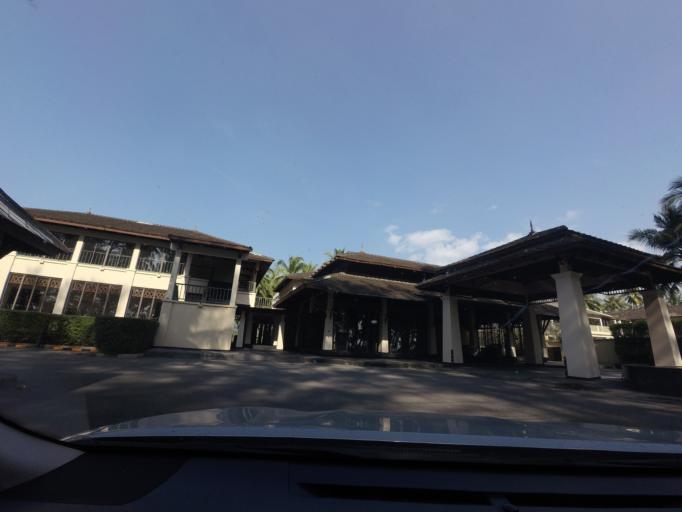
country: TH
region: Phangnga
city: Ban Khao Lak
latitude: 8.7242
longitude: 98.2316
